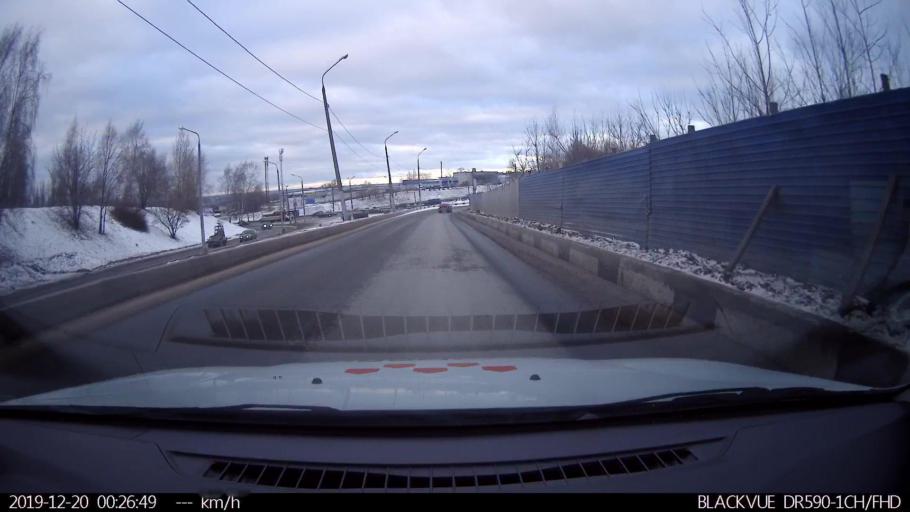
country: RU
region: Vladimir
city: Yur'yev-Pol'skiy
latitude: 56.6061
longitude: 39.5600
